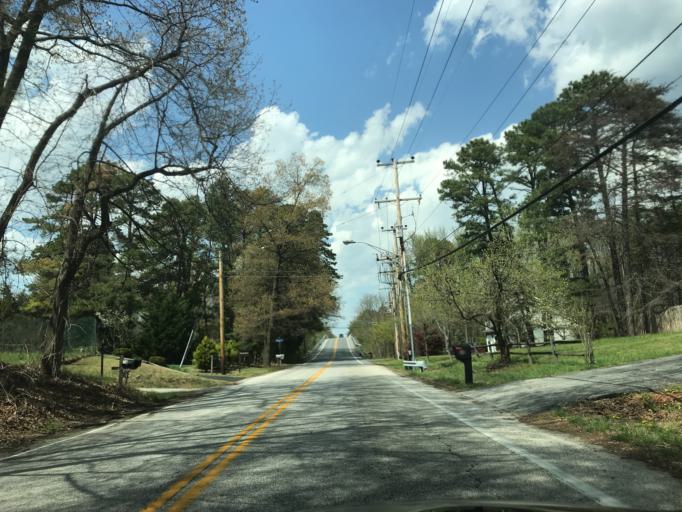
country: US
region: Maryland
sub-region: Anne Arundel County
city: Severn
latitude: 39.1526
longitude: -76.6692
